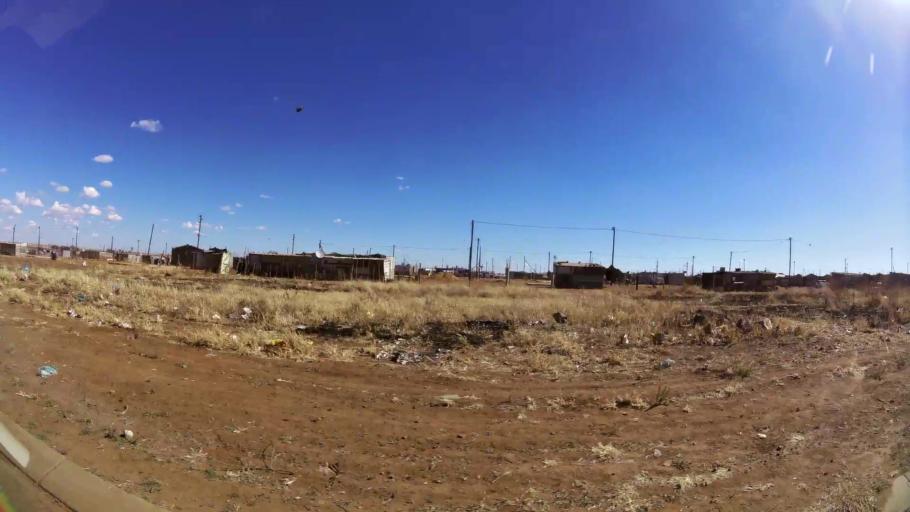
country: ZA
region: North-West
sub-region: Dr Kenneth Kaunda District Municipality
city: Klerksdorp
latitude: -26.8678
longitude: 26.5652
